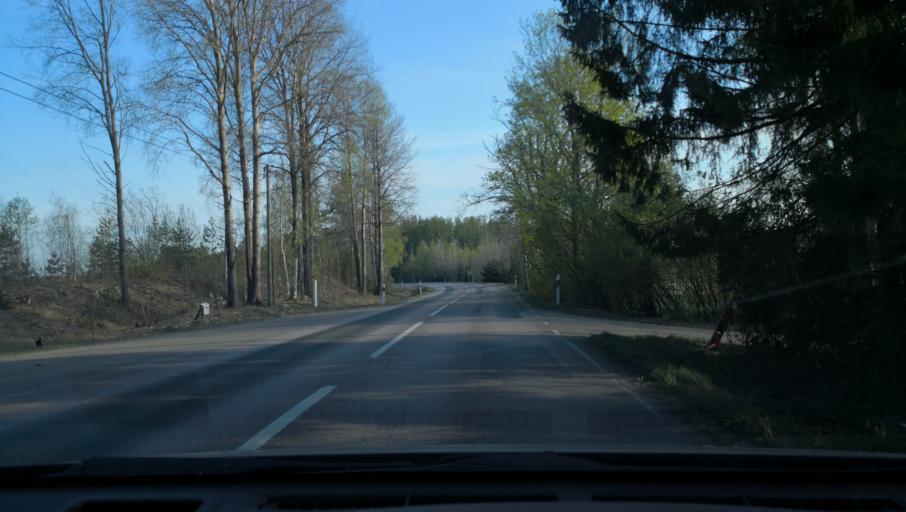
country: SE
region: Uppsala
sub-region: Heby Kommun
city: Heby
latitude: 59.9866
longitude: 16.8328
